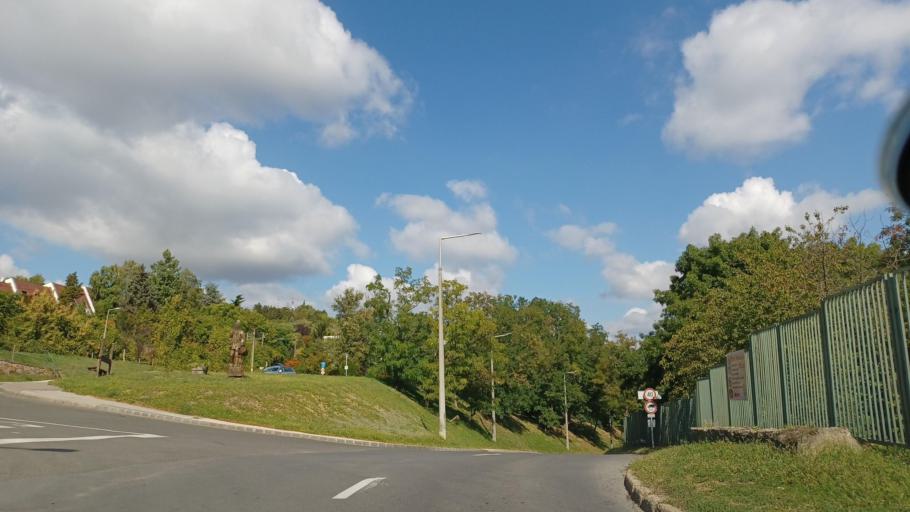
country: HU
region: Tolna
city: Szekszard
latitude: 46.3421
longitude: 18.6958
